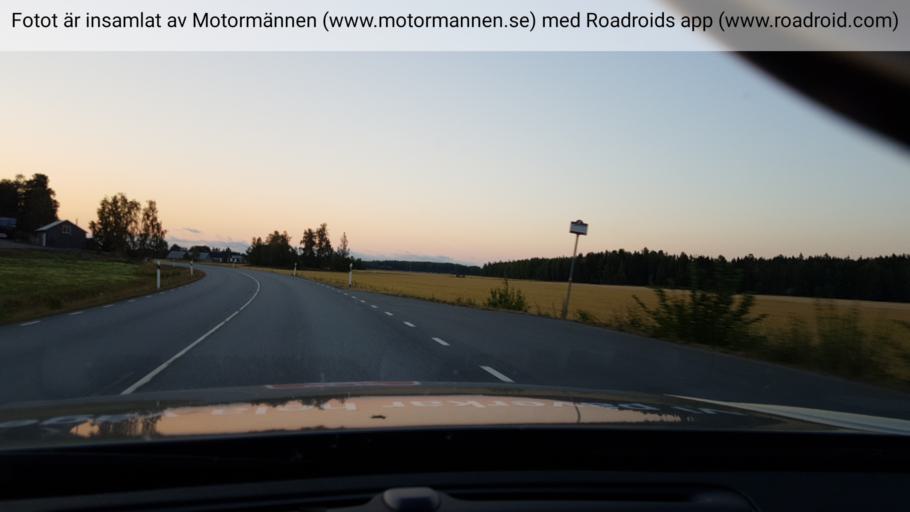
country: SE
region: Uppsala
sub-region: Heby Kommun
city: OEstervala
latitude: 60.1586
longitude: 17.2058
